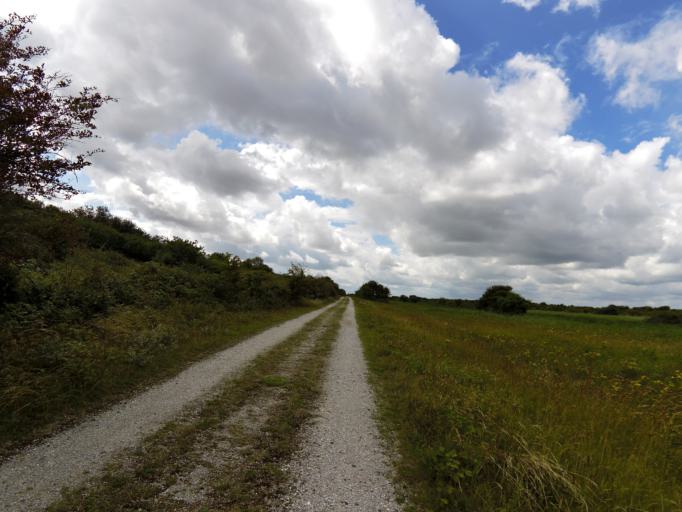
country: NL
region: South Holland
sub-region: Gemeente Goeree-Overflakkee
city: Goedereede
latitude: 51.8373
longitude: 3.9752
